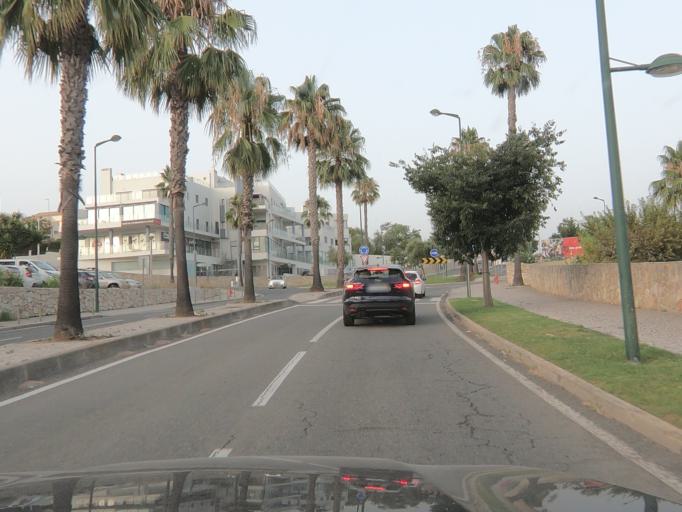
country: PT
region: Faro
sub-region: Loule
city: Loule
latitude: 37.1354
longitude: -8.0327
